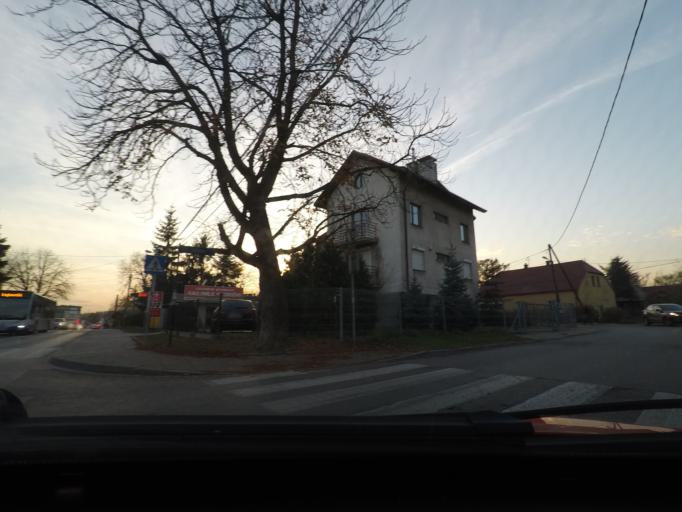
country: PL
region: Lesser Poland Voivodeship
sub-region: Krakow
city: Sidzina
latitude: 50.0213
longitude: 19.9087
